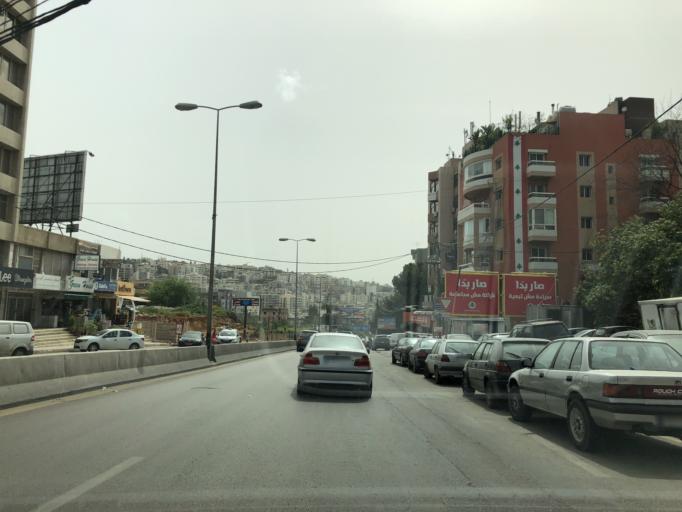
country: LB
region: Mont-Liban
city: Baabda
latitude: 33.8673
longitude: 35.5418
